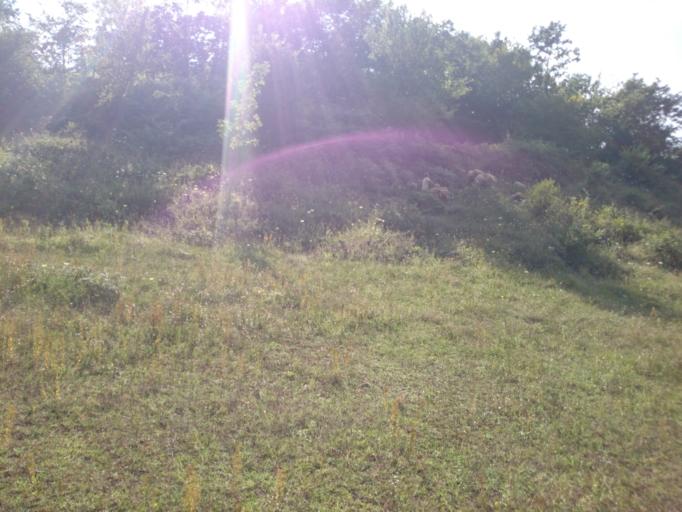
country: AL
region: Diber
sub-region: Rrethi i Dibres
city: Arras
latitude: 41.7420
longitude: 20.2837
